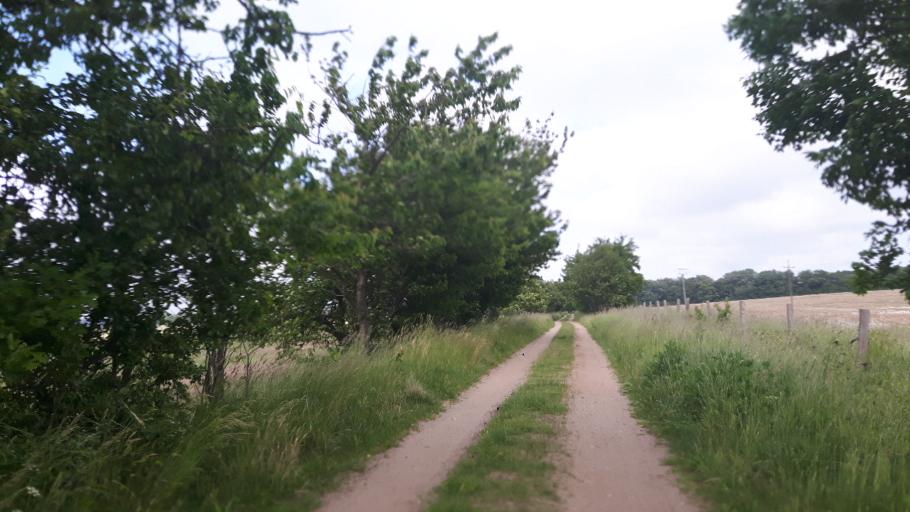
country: PL
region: Pomeranian Voivodeship
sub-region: Powiat slupski
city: Ustka
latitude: 54.5945
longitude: 16.9829
